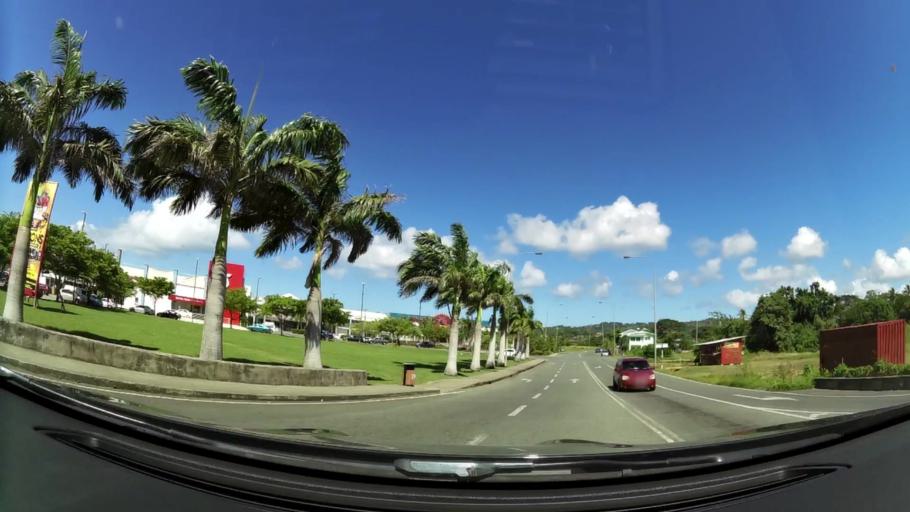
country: TT
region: Tobago
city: Scarborough
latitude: 11.1603
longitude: -60.7782
